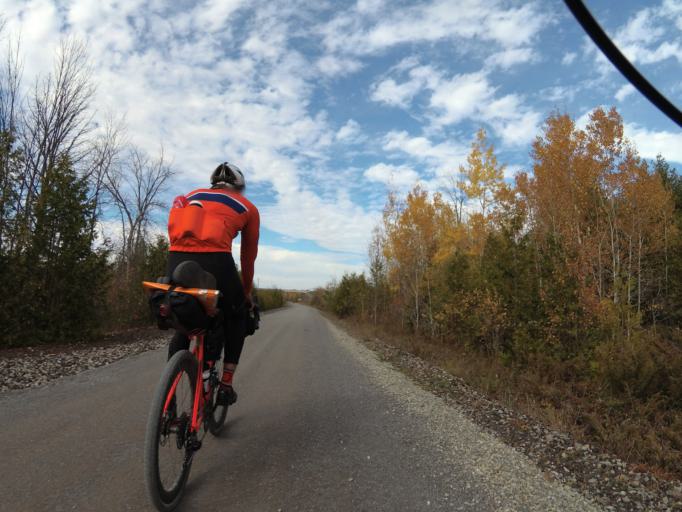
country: CA
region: Ontario
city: Carleton Place
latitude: 45.1338
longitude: -76.1365
